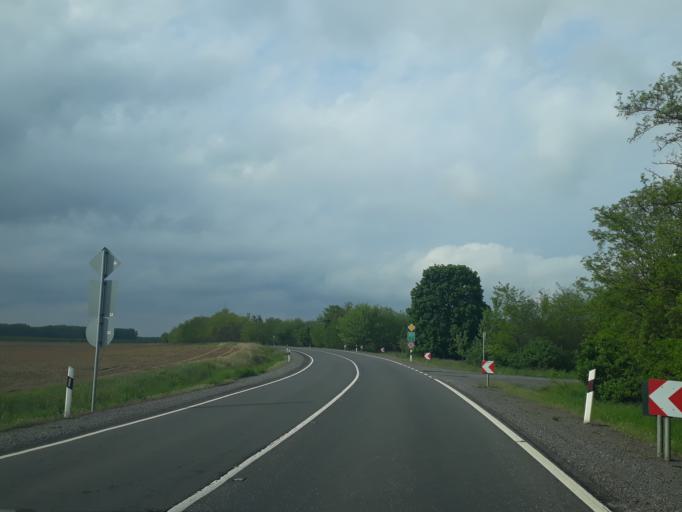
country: HU
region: Szabolcs-Szatmar-Bereg
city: Patroha
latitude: 48.1507
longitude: 22.0288
